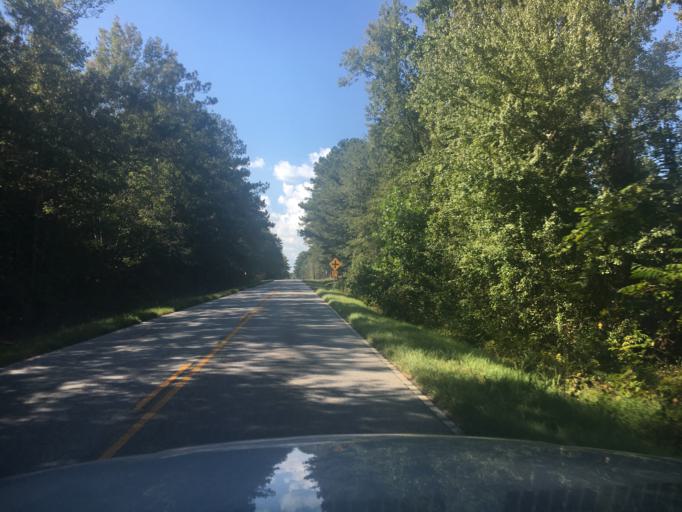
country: US
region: South Carolina
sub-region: Greenwood County
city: Greenwood
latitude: 34.2930
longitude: -82.2127
